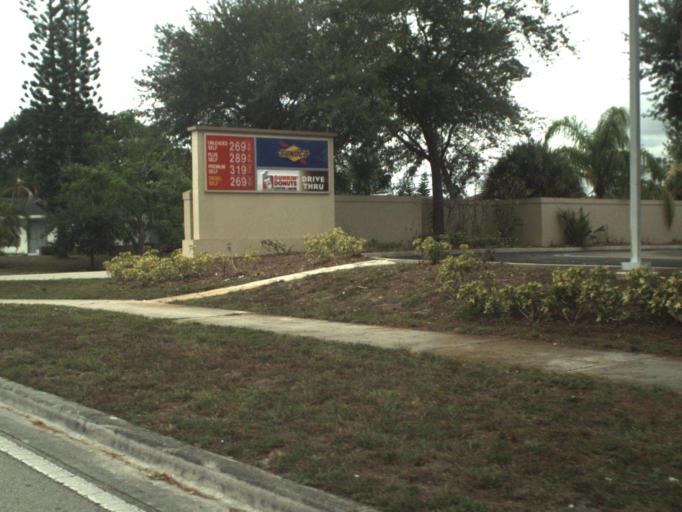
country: US
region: Florida
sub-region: Saint Lucie County
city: River Park
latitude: 27.3321
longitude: -80.3524
